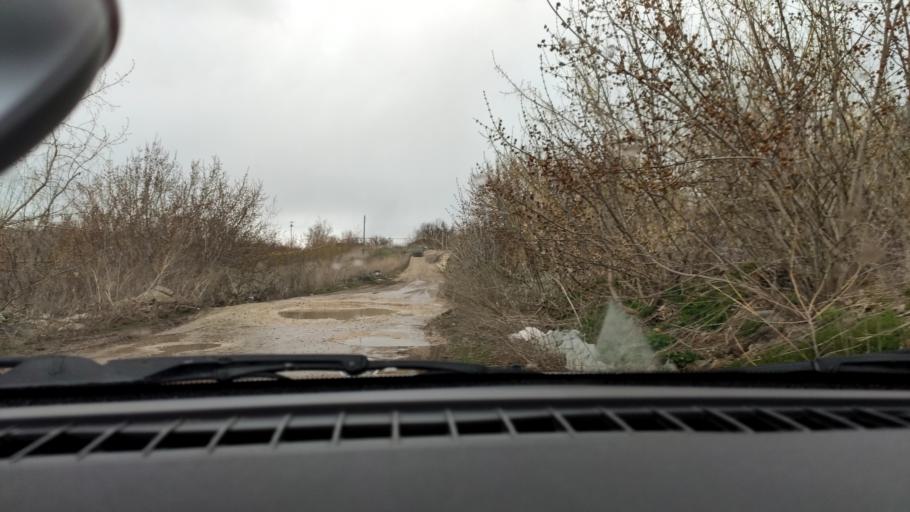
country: RU
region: Samara
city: Novosemeykino
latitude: 53.3237
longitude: 50.2925
